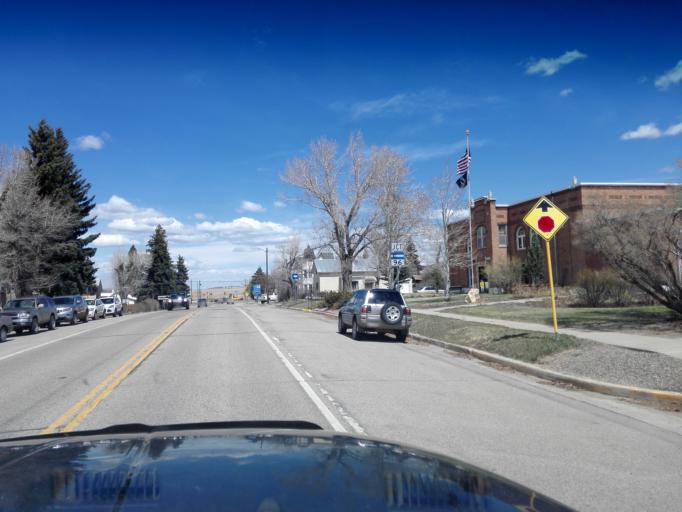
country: US
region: Colorado
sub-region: Custer County
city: Westcliffe
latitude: 38.1339
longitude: -105.4638
